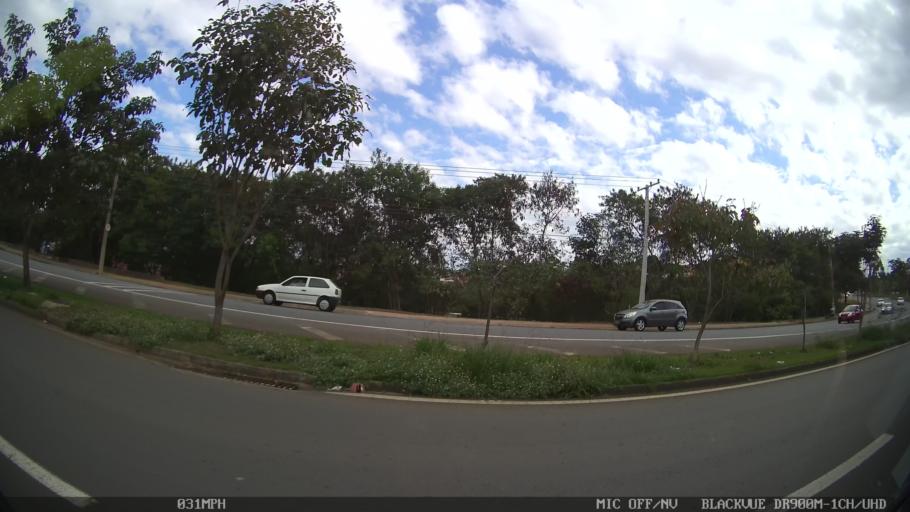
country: BR
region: Sao Paulo
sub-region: Limeira
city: Limeira
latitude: -22.5470
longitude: -47.3856
